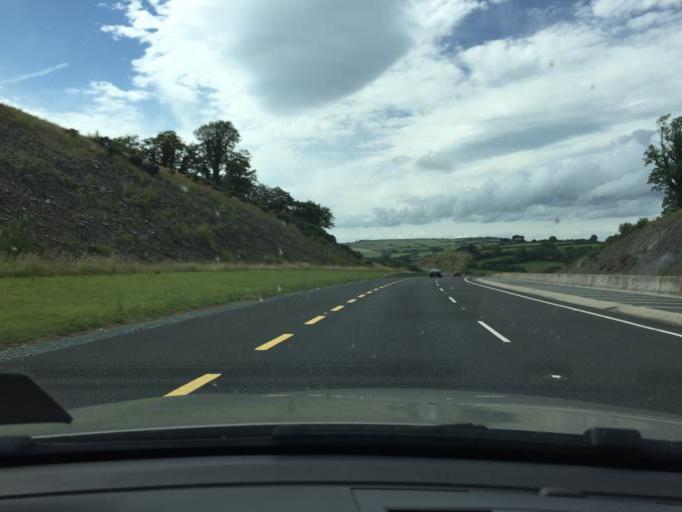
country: IE
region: Leinster
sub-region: Kilkenny
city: Mooncoin
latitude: 52.2359
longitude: -7.2327
